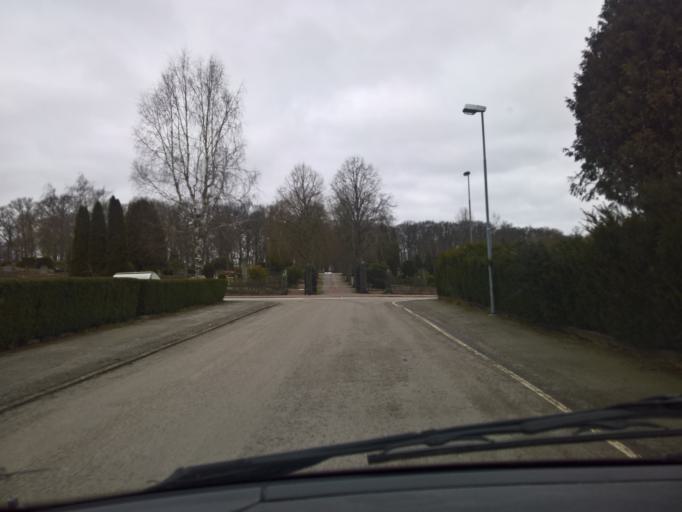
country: SE
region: Skane
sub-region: Hoors Kommun
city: Hoeoer
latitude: 55.9294
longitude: 13.5369
